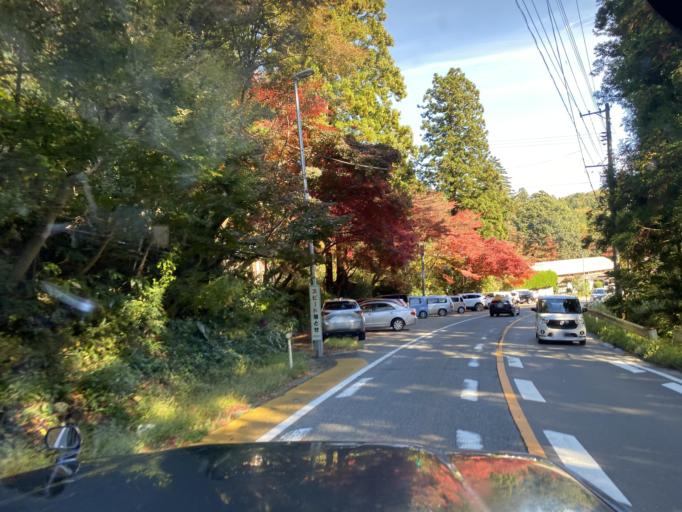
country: JP
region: Niigata
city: Niitsu-honcho
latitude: 37.7498
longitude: 139.1114
